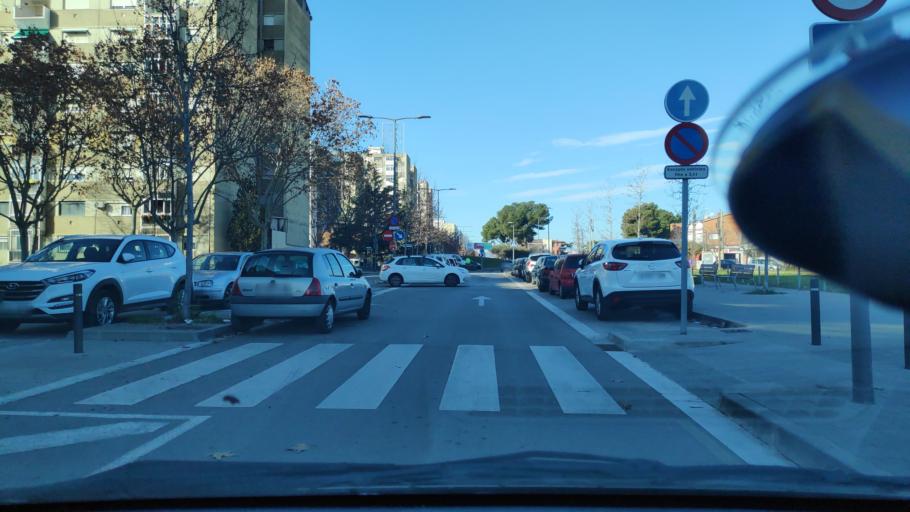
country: ES
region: Catalonia
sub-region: Provincia de Barcelona
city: Barbera del Valles
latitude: 41.5070
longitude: 2.1210
